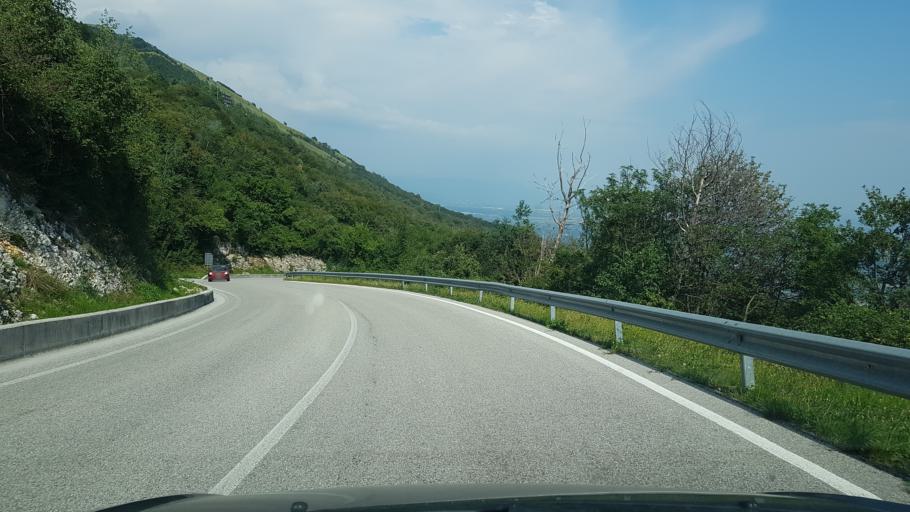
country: IT
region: Friuli Venezia Giulia
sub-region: Provincia di Pordenone
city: Budoia
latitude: 46.0776
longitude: 12.5389
